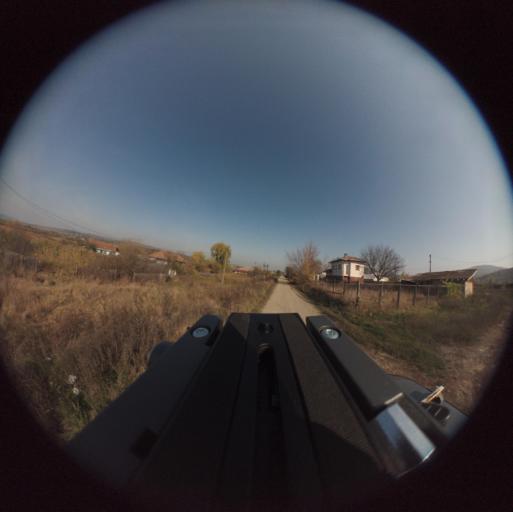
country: RO
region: Vaslui
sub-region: Comuna Dumesti
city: Dumesti
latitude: 46.8298
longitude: 27.2593
